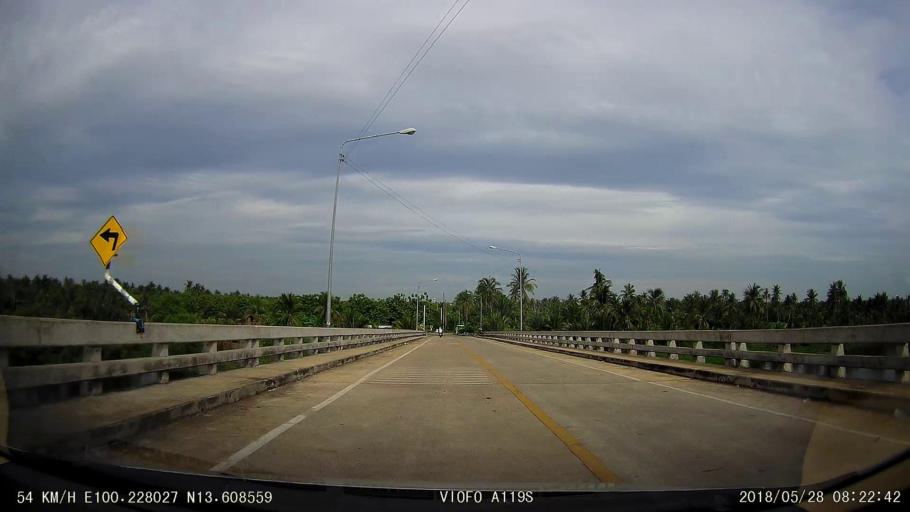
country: TH
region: Samut Sakhon
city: Krathum Baen
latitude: 13.6081
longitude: 100.2275
